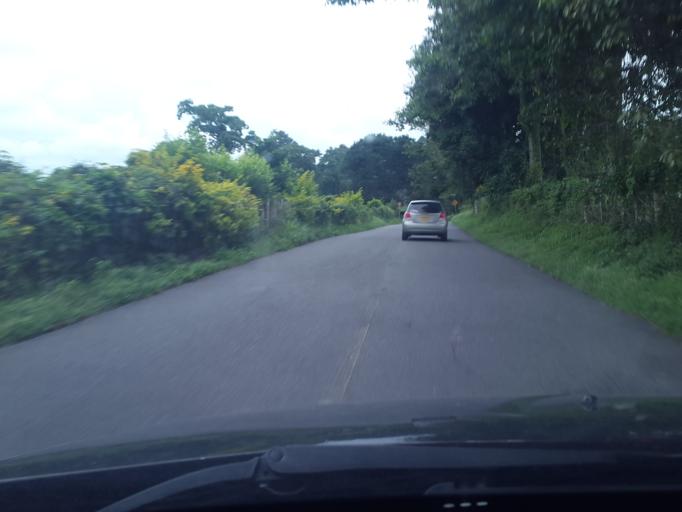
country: CO
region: Quindio
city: La Tebaida
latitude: 4.5049
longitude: -75.7902
